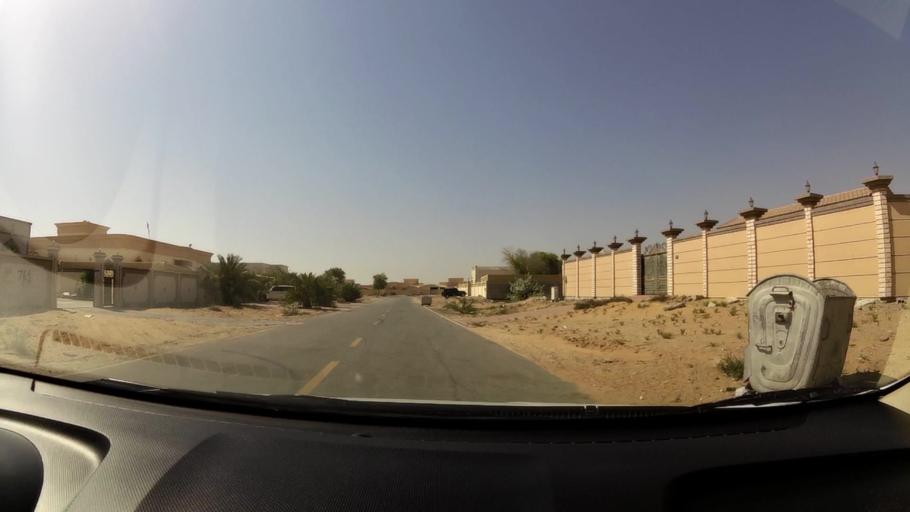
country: AE
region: Umm al Qaywayn
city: Umm al Qaywayn
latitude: 25.4756
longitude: 55.6158
